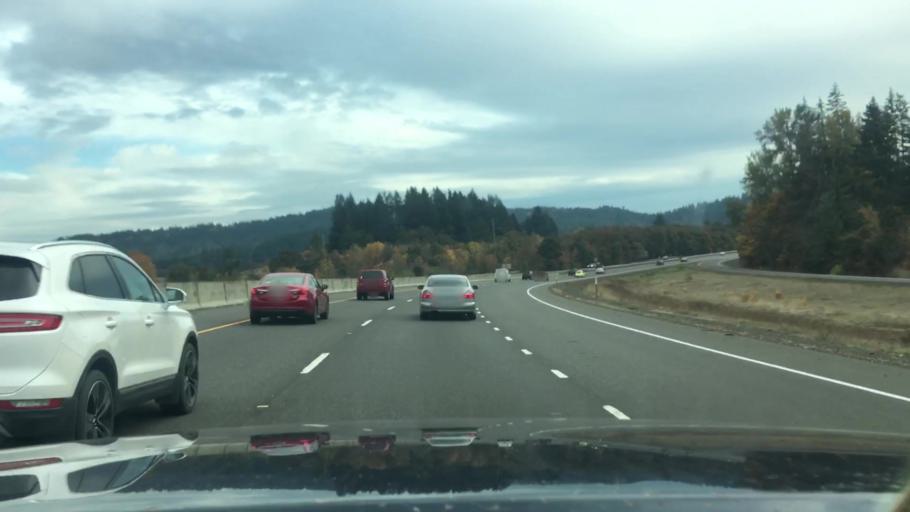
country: US
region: Oregon
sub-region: Lane County
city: Springfield
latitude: 43.9959
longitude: -123.0053
